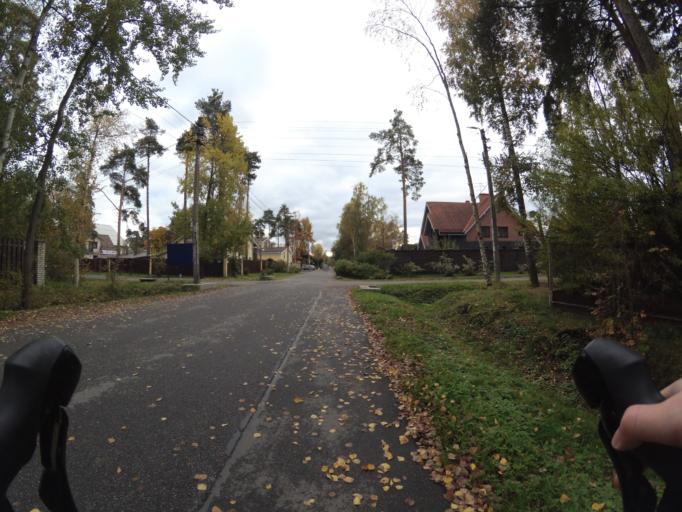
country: RU
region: St.-Petersburg
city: Lakhtinskiy
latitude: 59.9997
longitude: 30.1322
